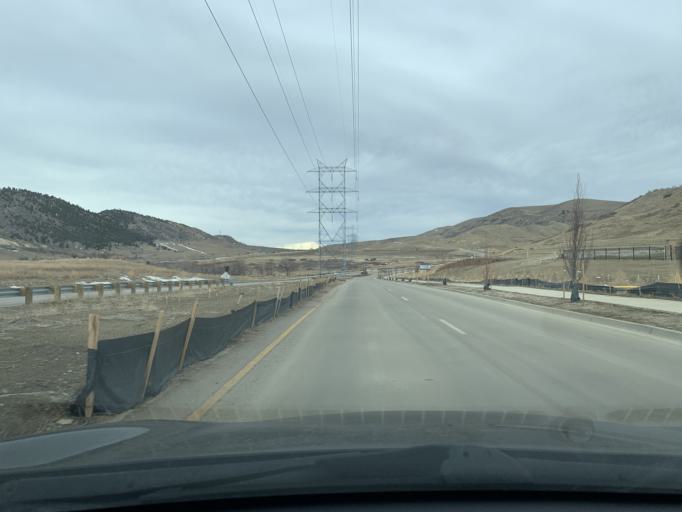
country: US
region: Colorado
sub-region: Jefferson County
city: West Pleasant View
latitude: 39.6765
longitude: -105.1832
